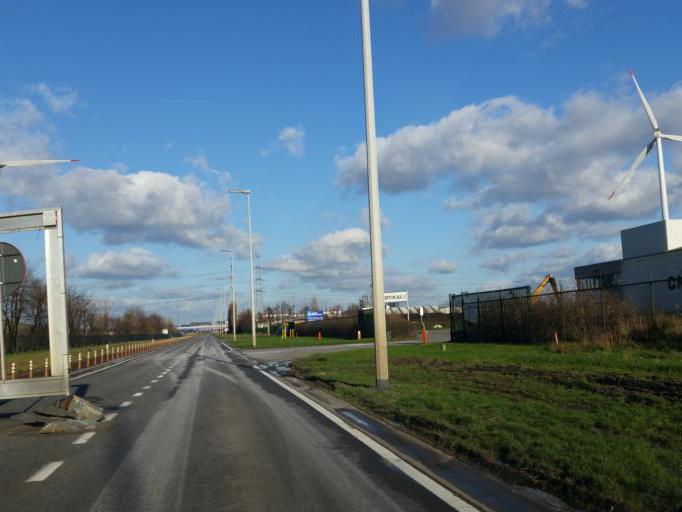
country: BE
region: Flanders
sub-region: Provincie Oost-Vlaanderen
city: Beveren
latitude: 51.2817
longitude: 4.2757
